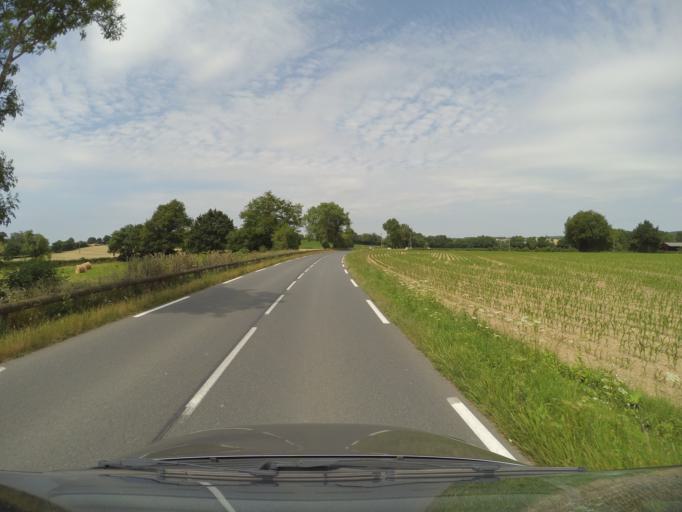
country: FR
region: Pays de la Loire
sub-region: Departement de la Vendee
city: Saint-Paul-en-Pareds
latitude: 46.8505
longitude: -0.9507
